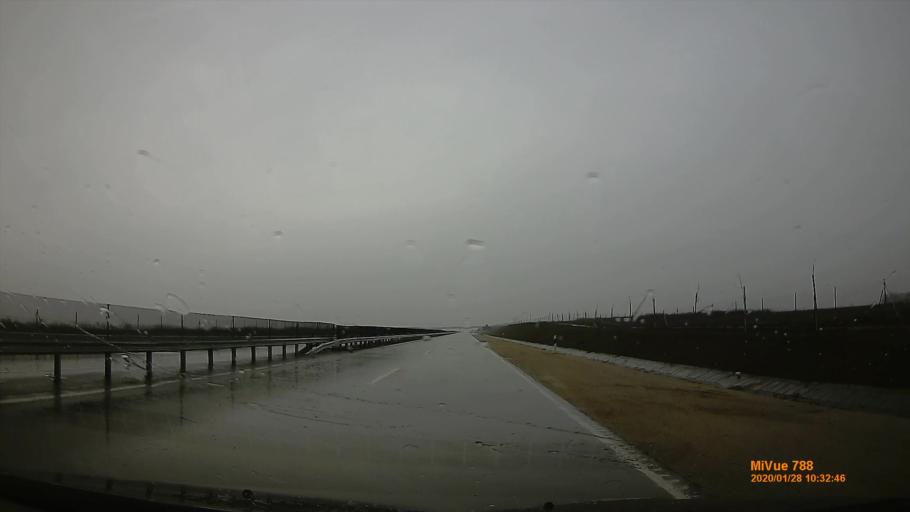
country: HU
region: Pest
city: Monor
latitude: 47.3528
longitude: 19.4902
